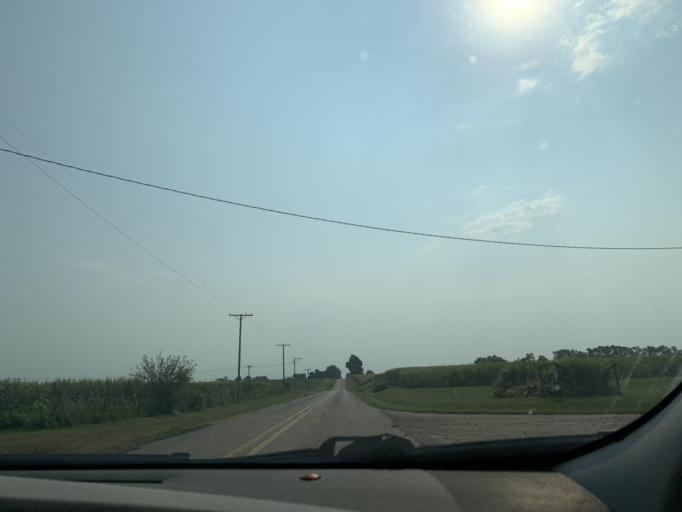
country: US
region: Illinois
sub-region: Carroll County
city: Milledgeville
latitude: 41.8480
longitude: -89.8351
